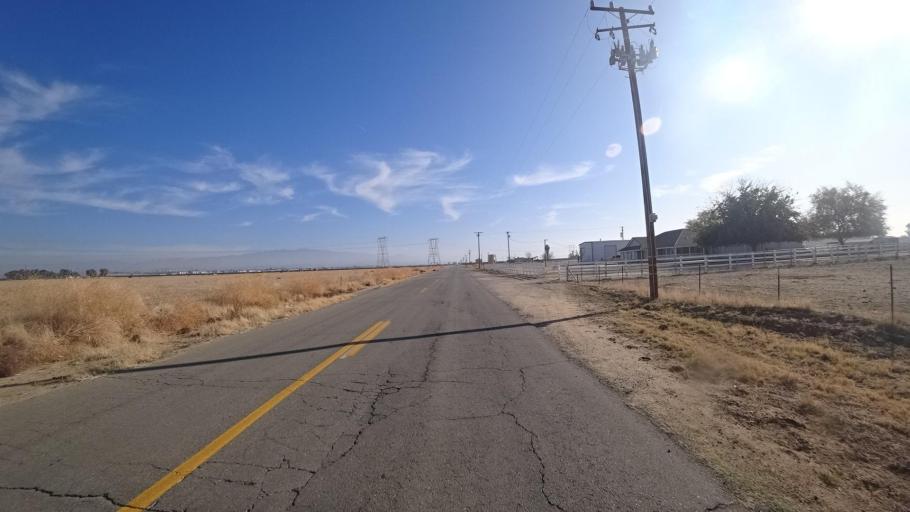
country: US
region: California
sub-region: Kern County
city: Lamont
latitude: 35.3399
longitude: -118.9045
